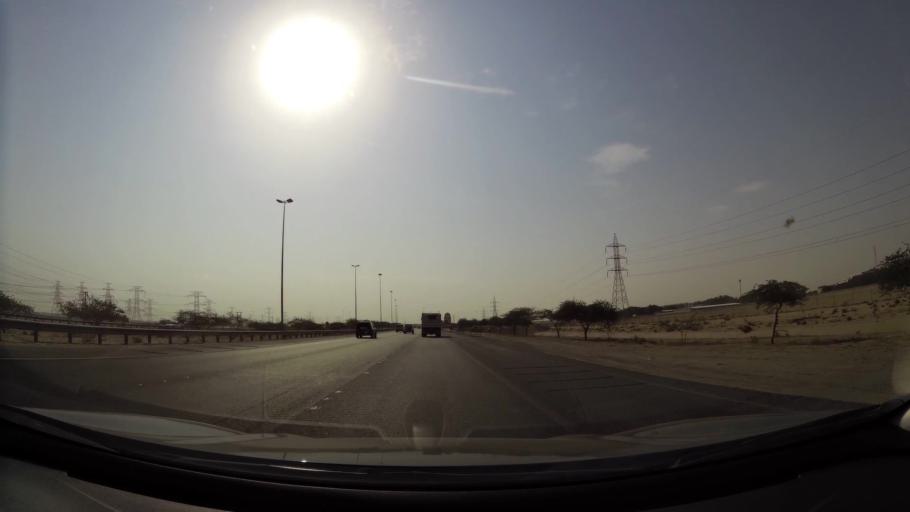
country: KW
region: Al Ahmadi
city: Al Ahmadi
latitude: 28.9666
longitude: 48.1163
